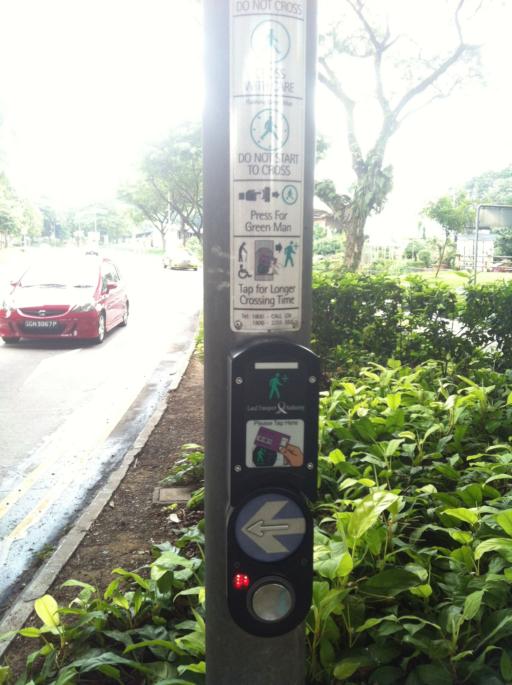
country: SG
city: Singapore
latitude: 1.3405
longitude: 103.8370
